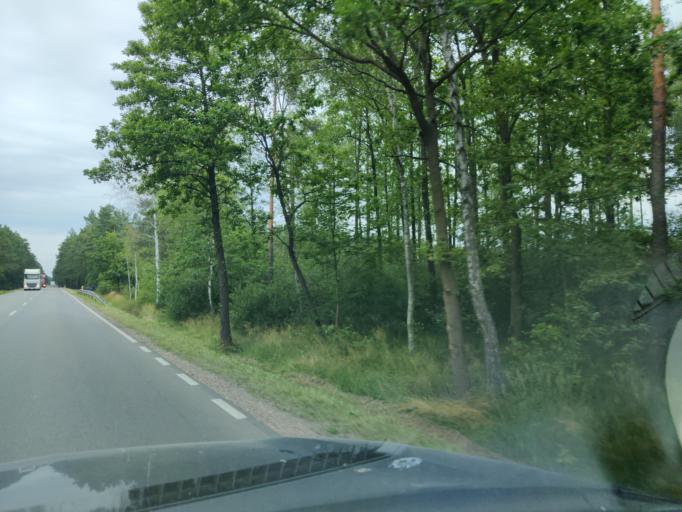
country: PL
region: Masovian Voivodeship
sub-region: Powiat minski
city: Stanislawow
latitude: 52.3431
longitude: 21.5793
